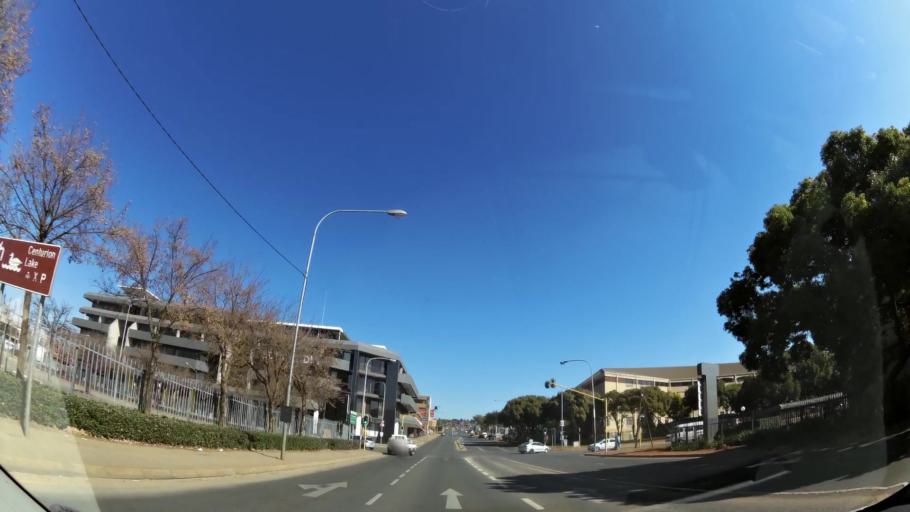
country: ZA
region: Gauteng
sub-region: City of Tshwane Metropolitan Municipality
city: Centurion
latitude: -25.8543
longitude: 28.1853
